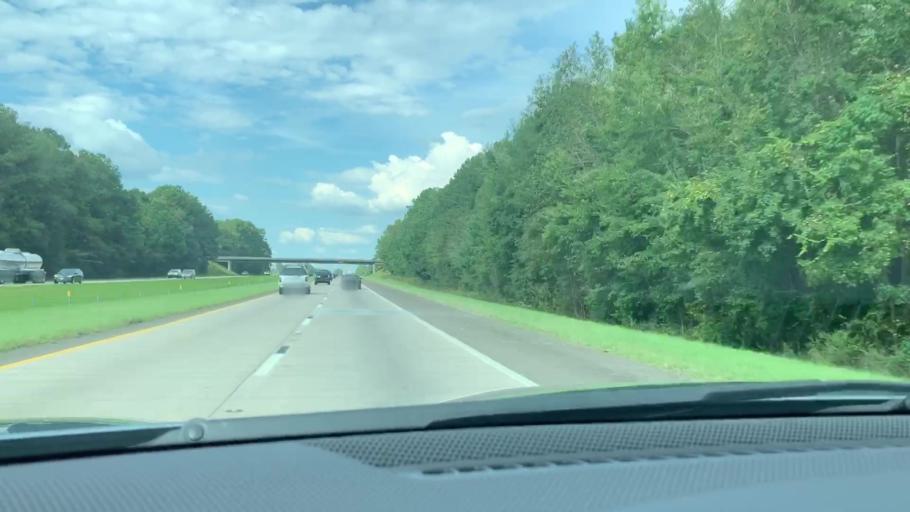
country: US
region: South Carolina
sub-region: Hampton County
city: Yemassee
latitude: 32.6760
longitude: -80.8825
